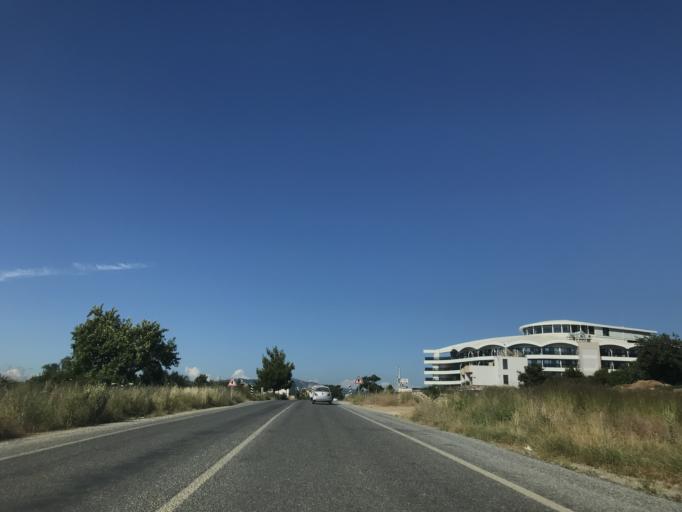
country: TR
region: Aydin
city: Davutlar
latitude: 37.7265
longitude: 27.2626
